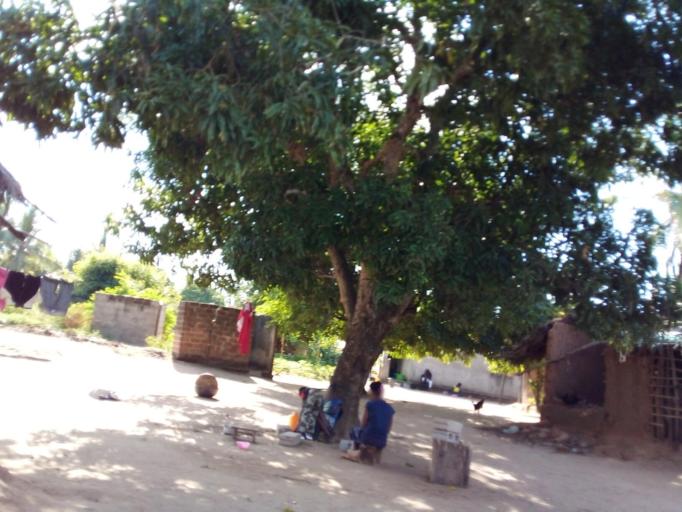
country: MZ
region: Zambezia
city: Quelimane
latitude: -17.5749
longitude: 36.7024
